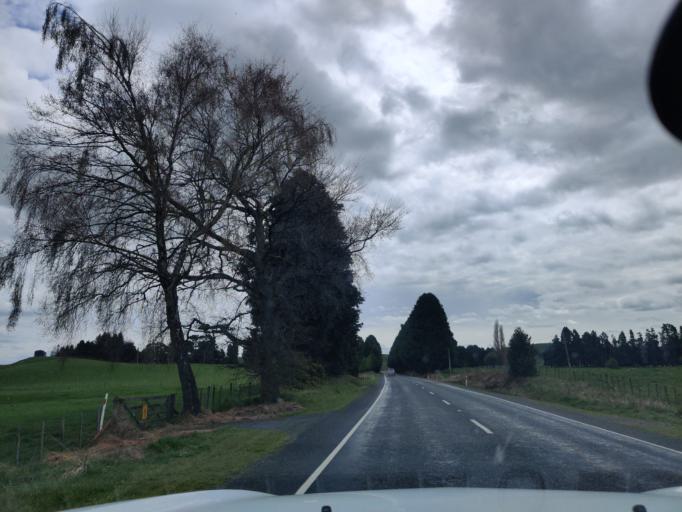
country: NZ
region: Manawatu-Wanganui
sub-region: Ruapehu District
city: Waiouru
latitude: -39.3912
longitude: 175.3675
